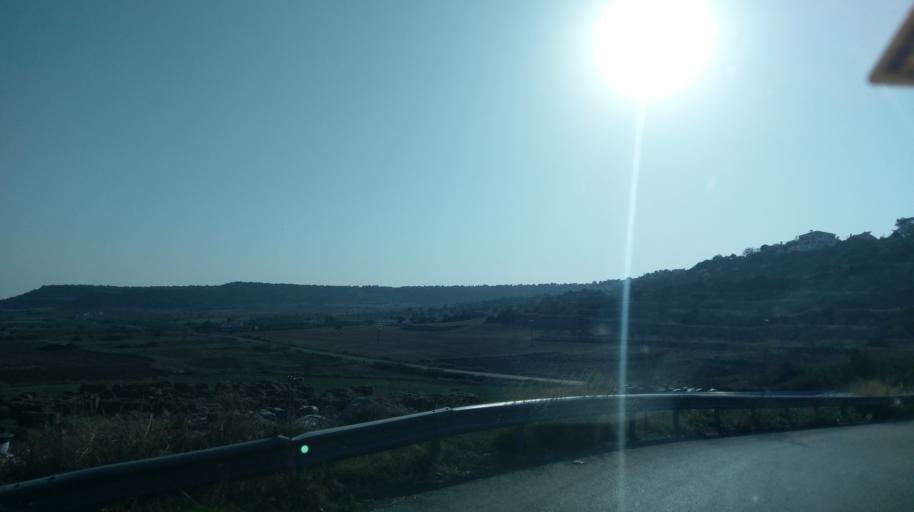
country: CY
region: Ammochostos
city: Leonarisso
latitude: 35.4199
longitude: 34.0744
